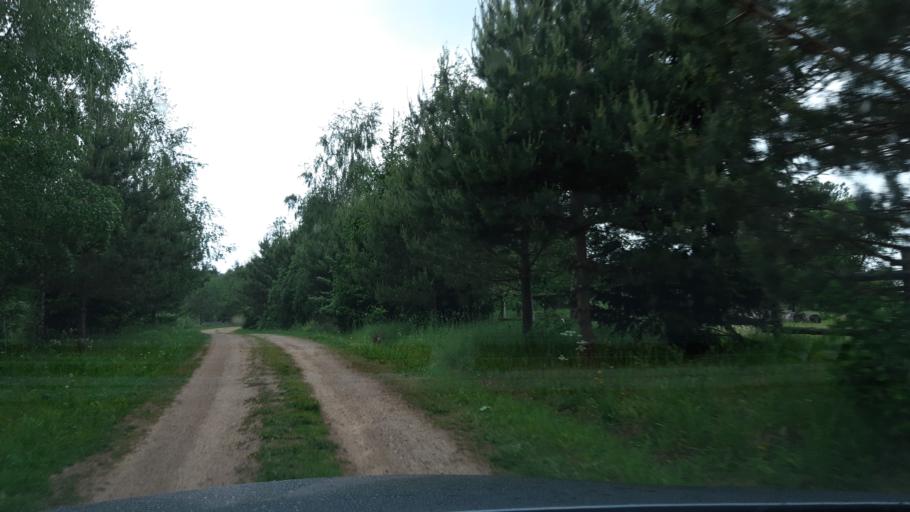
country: LT
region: Utenos apskritis
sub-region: Anyksciai
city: Anyksciai
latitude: 55.4457
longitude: 25.1977
